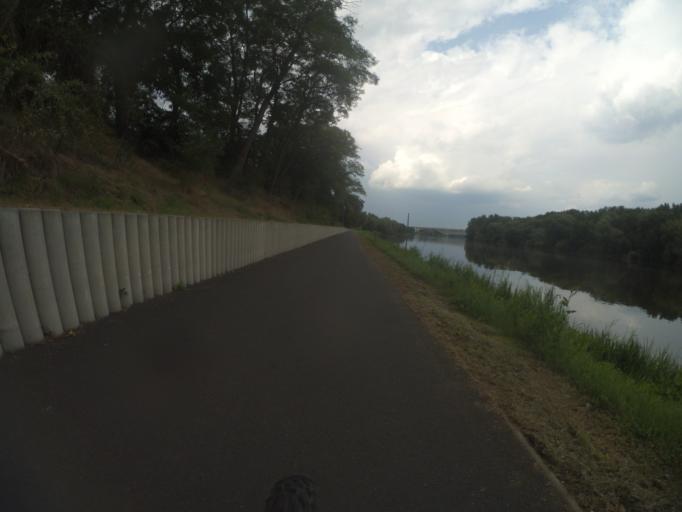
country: CZ
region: Central Bohemia
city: Dolni Berkovice
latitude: 50.3763
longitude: 14.4503
